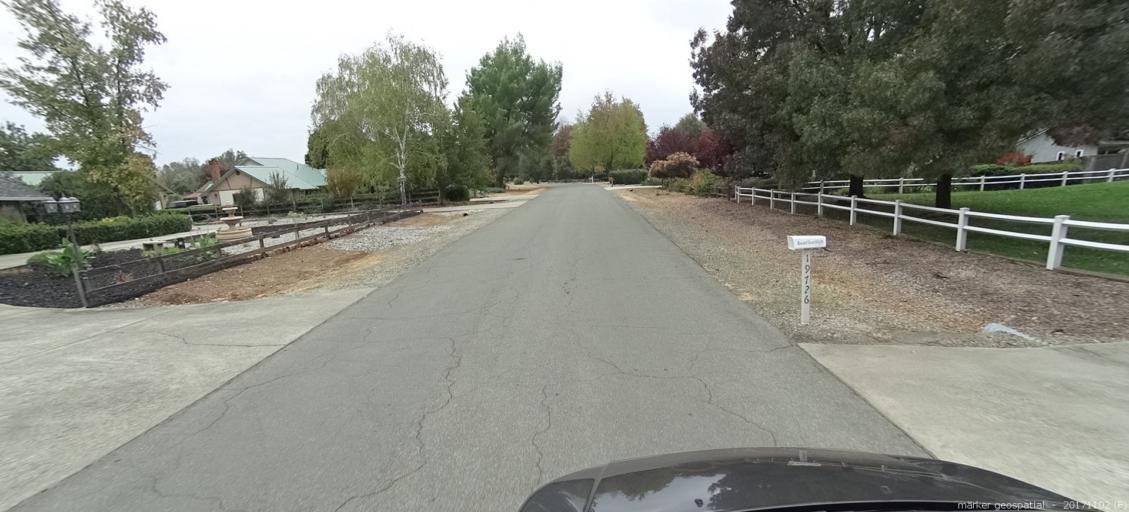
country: US
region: California
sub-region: Shasta County
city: Shasta Lake
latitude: 40.6573
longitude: -122.3274
